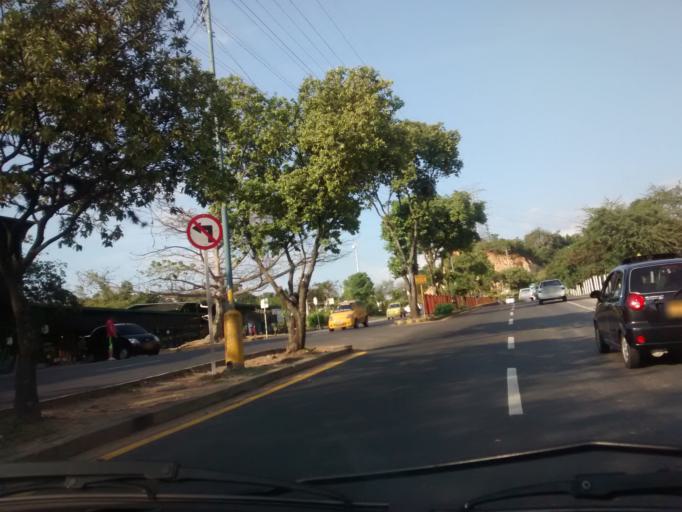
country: CO
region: Santander
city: Bucaramanga
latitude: 7.0929
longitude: -73.1305
